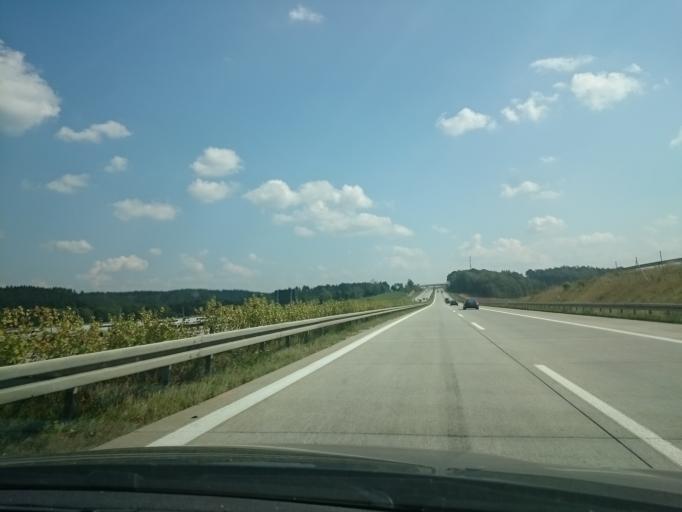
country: DE
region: Saxony
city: Wildenfels
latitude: 50.6851
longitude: 12.6206
